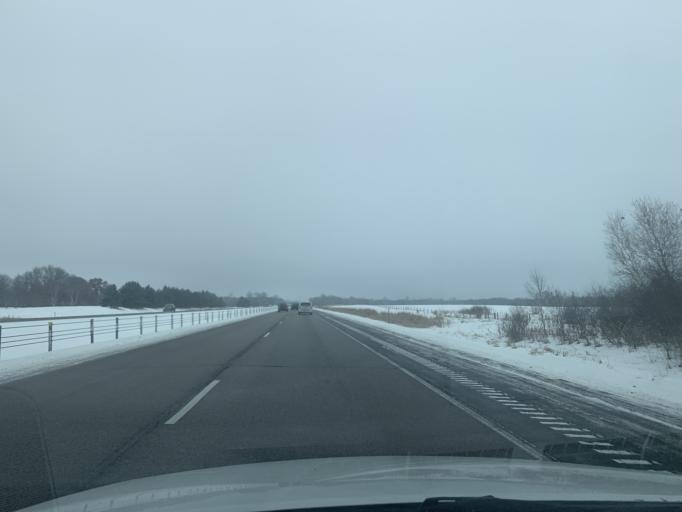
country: US
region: Minnesota
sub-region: Chisago County
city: Branch
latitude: 45.4737
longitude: -92.9963
